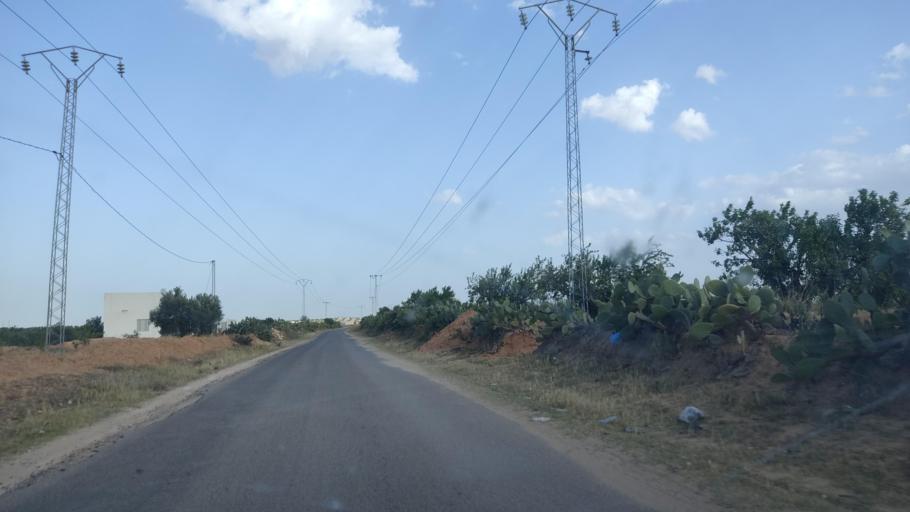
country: TN
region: Safaqis
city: Sfax
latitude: 34.8554
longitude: 10.6064
